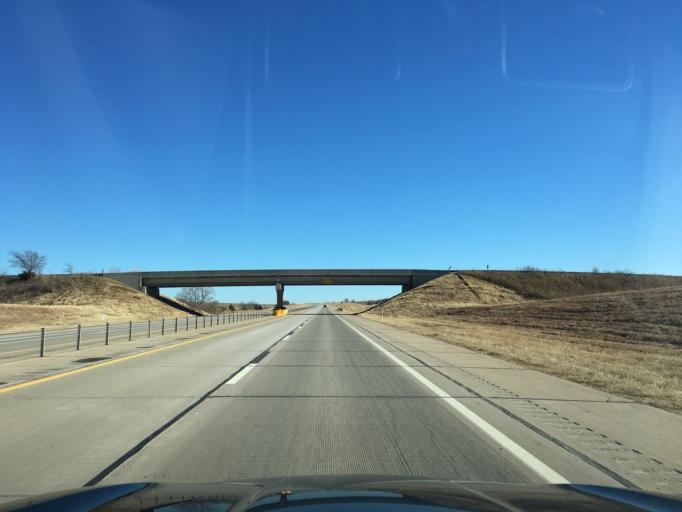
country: US
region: Oklahoma
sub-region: Noble County
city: Perry
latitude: 36.3928
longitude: -97.1947
